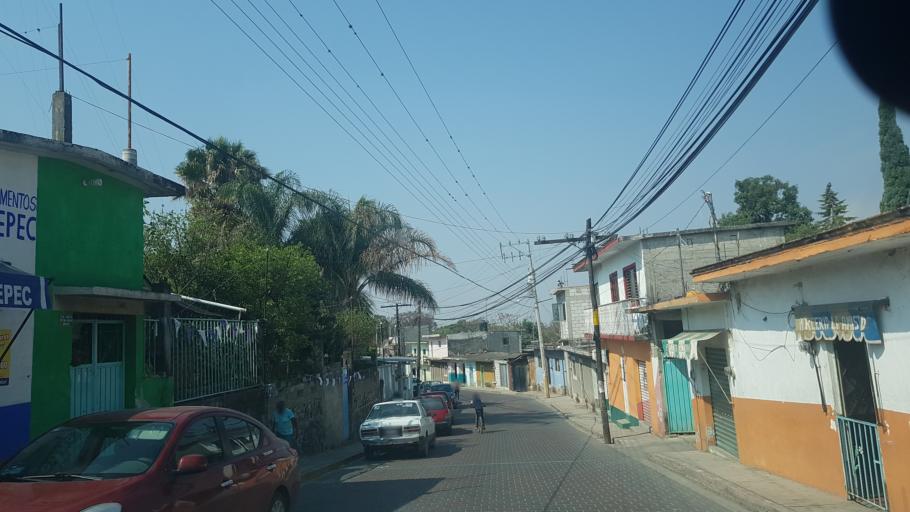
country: MX
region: Morelos
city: Tlacotepec
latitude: 18.8154
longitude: -98.7506
